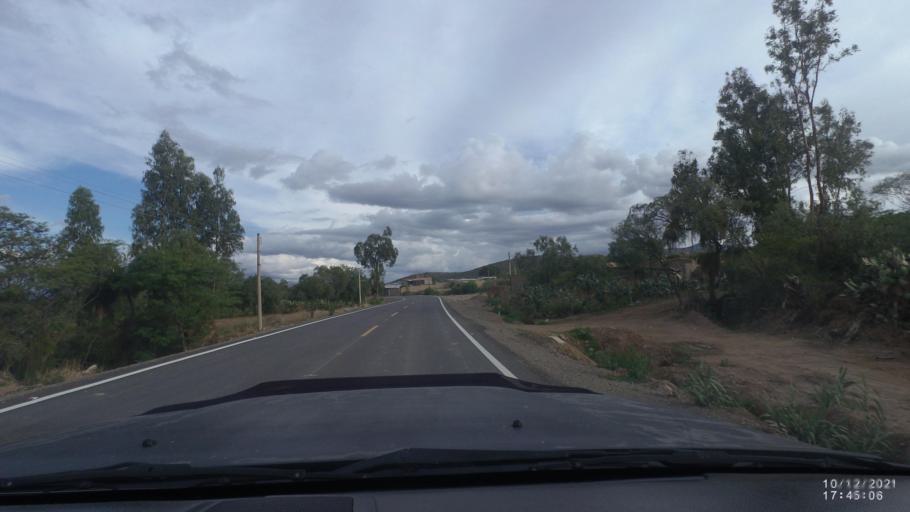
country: BO
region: Cochabamba
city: Tarata
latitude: -17.6246
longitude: -66.0062
